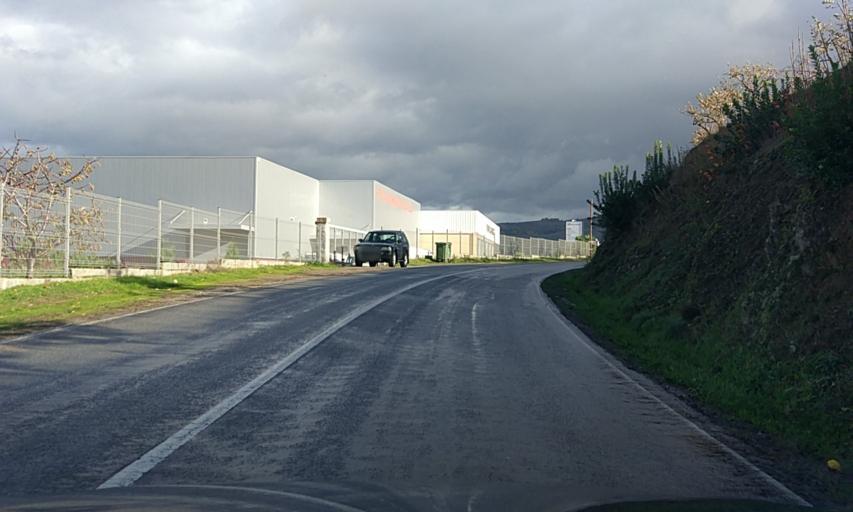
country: PT
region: Viseu
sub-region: Lamego
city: Lamego
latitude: 41.1107
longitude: -7.7917
